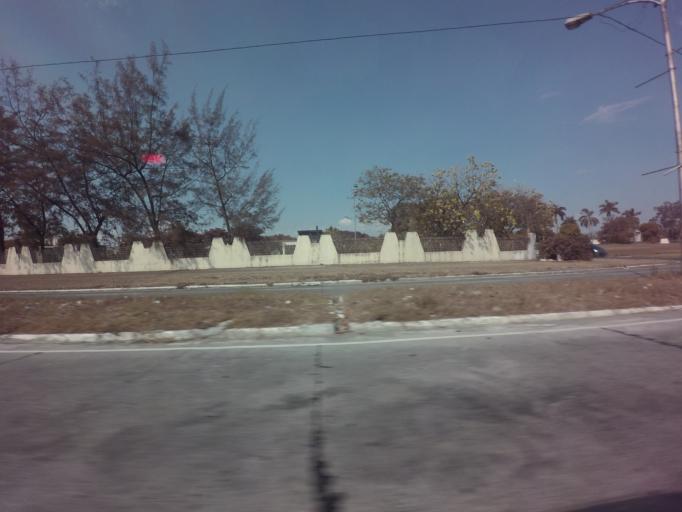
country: PH
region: Calabarzon
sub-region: Province of Rizal
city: Pateros
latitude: 14.5199
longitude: 121.0471
